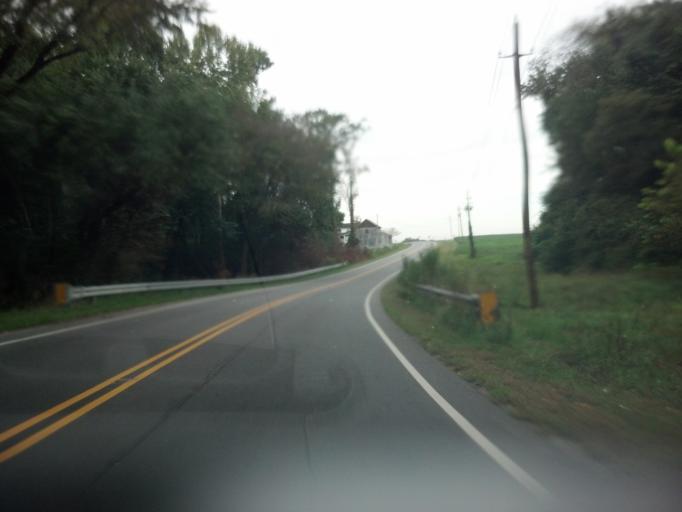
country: US
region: North Carolina
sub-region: Pitt County
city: Ayden
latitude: 35.4729
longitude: -77.4712
